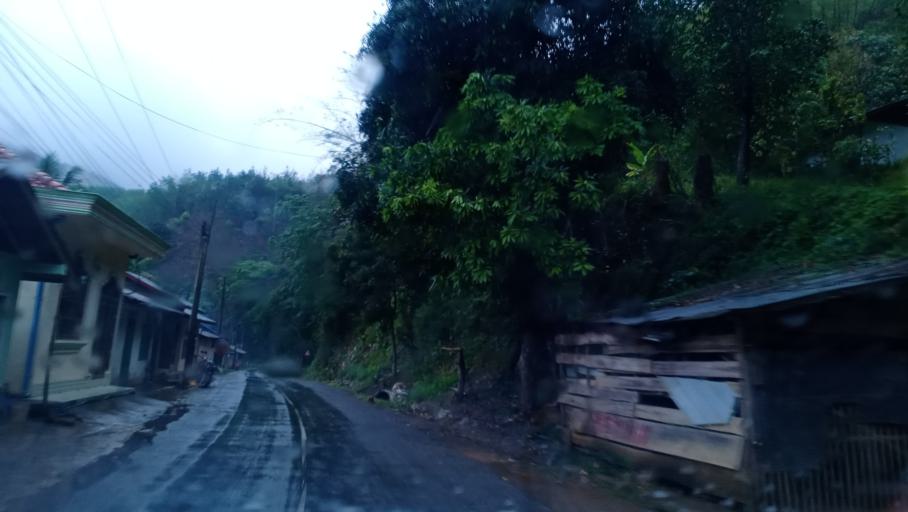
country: LA
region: Phongsali
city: Khoa
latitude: 21.0784
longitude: 102.5008
